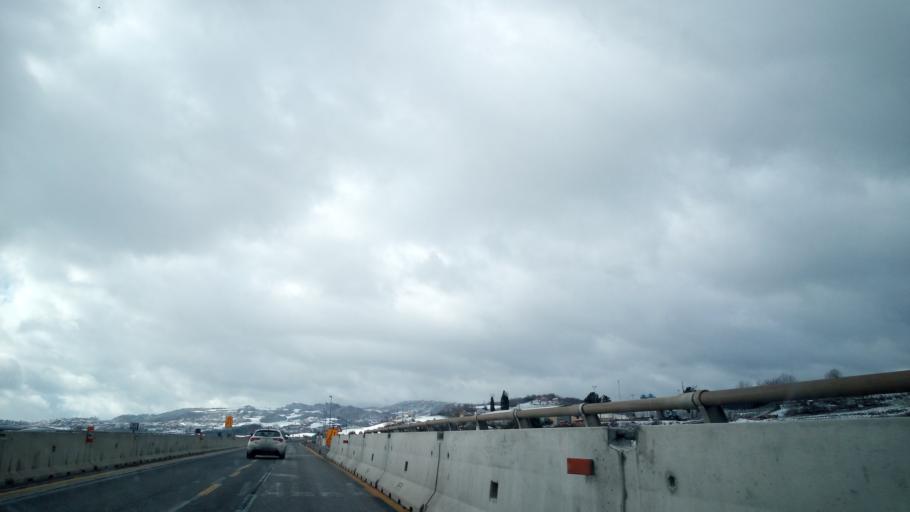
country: IT
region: Campania
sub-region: Provincia di Avellino
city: Scampitella
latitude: 41.0609
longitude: 15.2953
